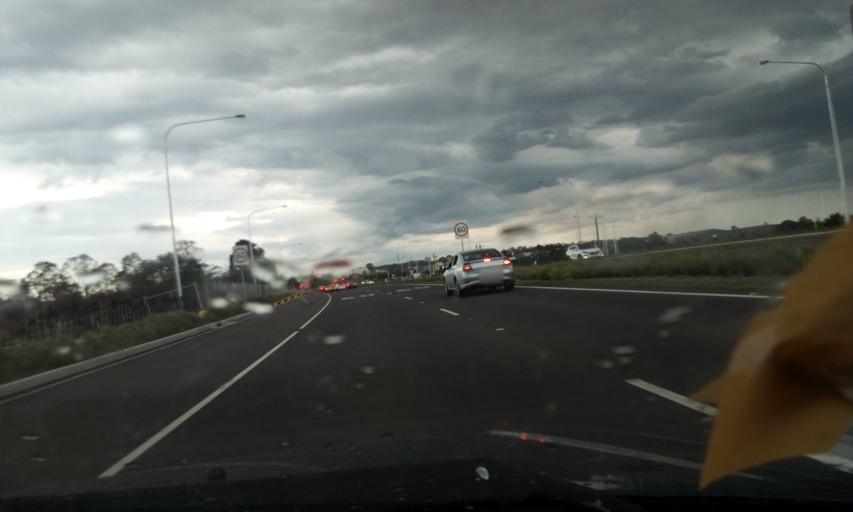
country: AU
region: New South Wales
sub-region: Camden
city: Narellan
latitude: -34.0295
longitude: 150.7277
